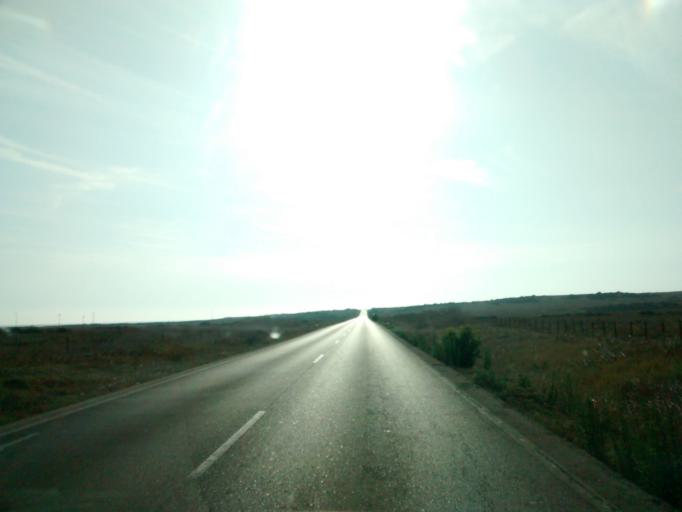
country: ES
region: Andalusia
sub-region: Provincia de Cadiz
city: Zahara de los Atunes
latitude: 36.1670
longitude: -5.8735
